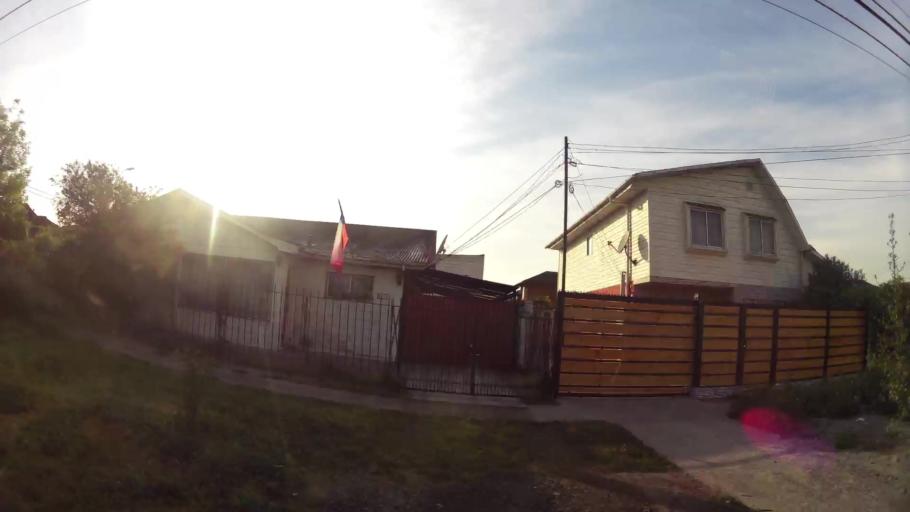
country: CL
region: Santiago Metropolitan
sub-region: Provincia de Santiago
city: La Pintana
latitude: -33.5284
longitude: -70.6705
